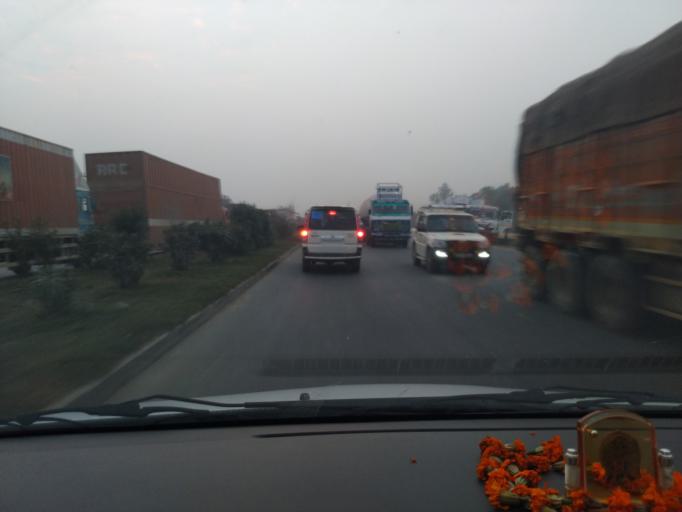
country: IN
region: Uttar Pradesh
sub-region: Ghazipur
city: Zamania
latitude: 25.2255
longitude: 83.4825
